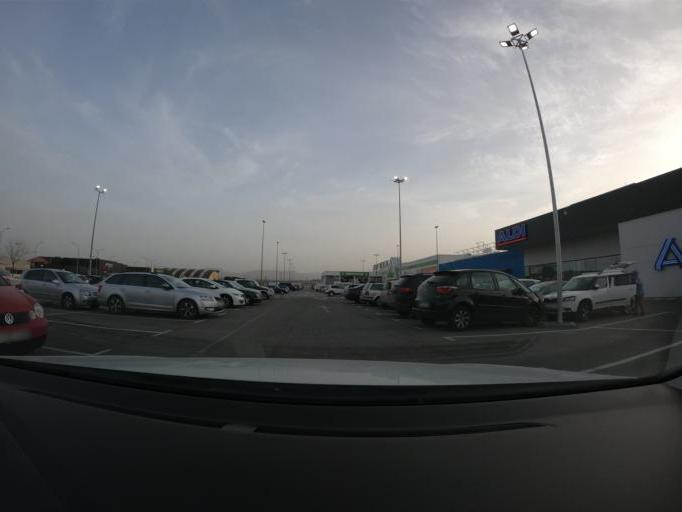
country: ES
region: La Rioja
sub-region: Provincia de La Rioja
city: Logrono
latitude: 42.4528
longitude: -2.4719
